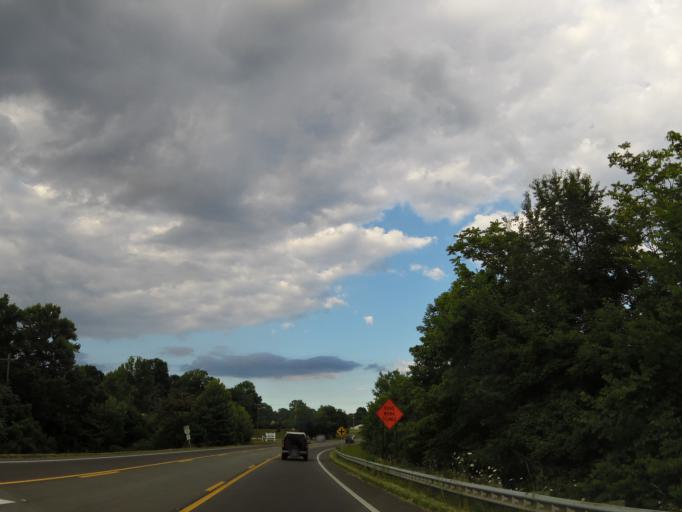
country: US
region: Tennessee
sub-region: Maury County
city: Columbia
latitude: 35.6356
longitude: -87.0071
